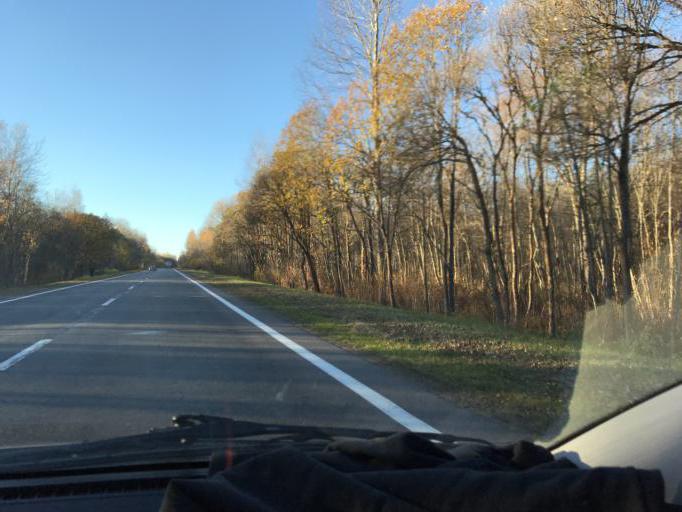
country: BY
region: Vitebsk
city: Vitebsk
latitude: 55.3562
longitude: 30.1842
